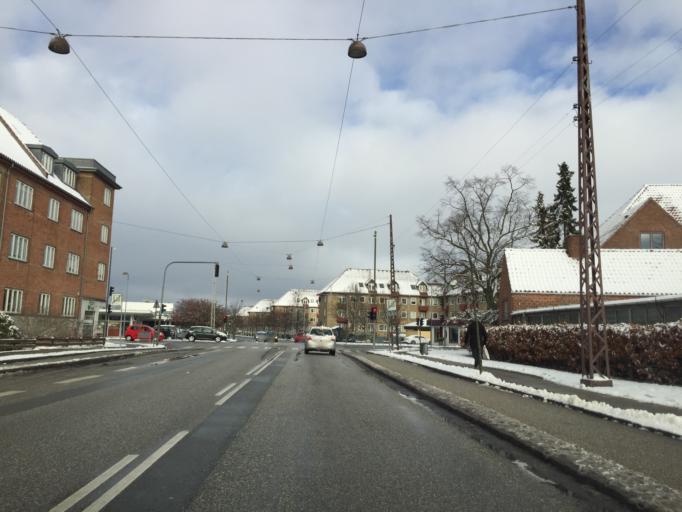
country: DK
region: Capital Region
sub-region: Tarnby Kommune
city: Tarnby
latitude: 55.6369
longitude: 12.6364
